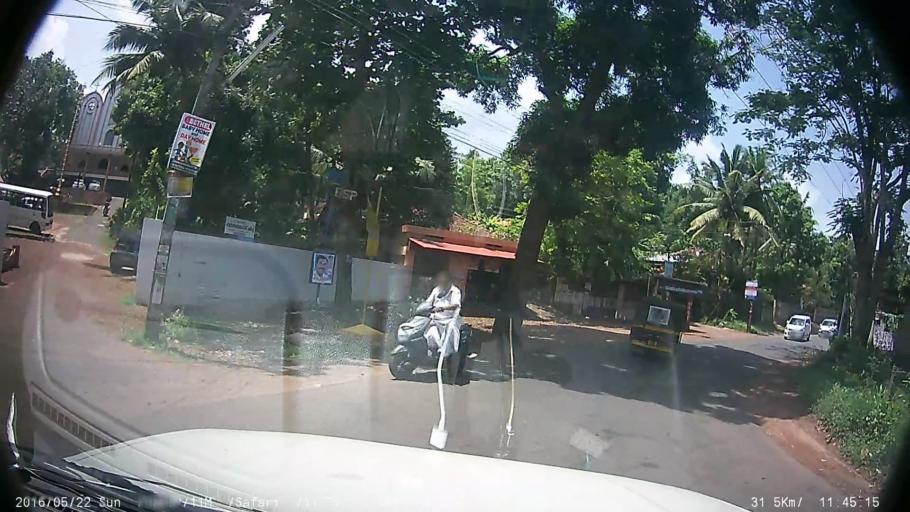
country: IN
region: Kerala
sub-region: Kottayam
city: Kottayam
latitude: 9.5408
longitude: 76.5211
